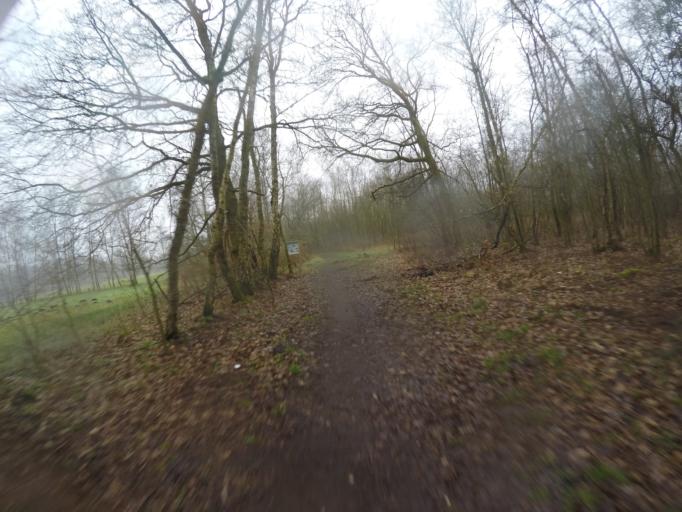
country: DE
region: Schleswig-Holstein
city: Quickborn
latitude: 53.7199
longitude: 9.9318
